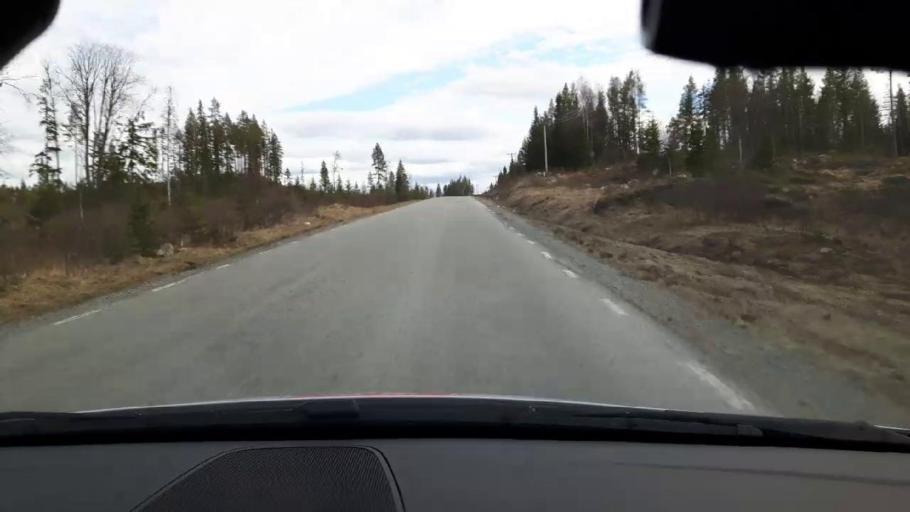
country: SE
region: Jaemtland
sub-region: Bergs Kommun
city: Hoverberg
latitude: 62.6988
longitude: 14.6236
